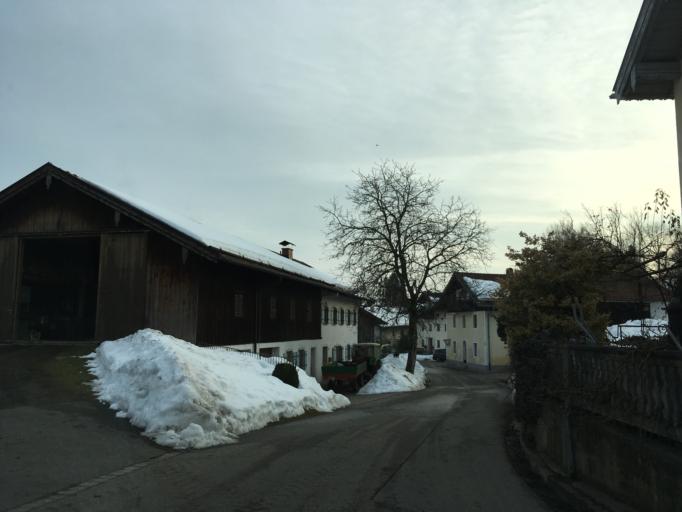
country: DE
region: Bavaria
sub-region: Upper Bavaria
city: Rimsting
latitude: 47.9120
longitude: 12.3348
